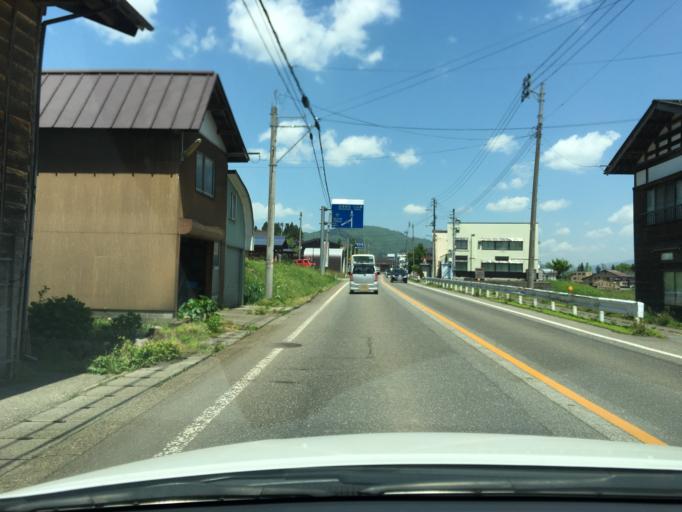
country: JP
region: Niigata
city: Ojiya
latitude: 37.2675
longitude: 138.9748
